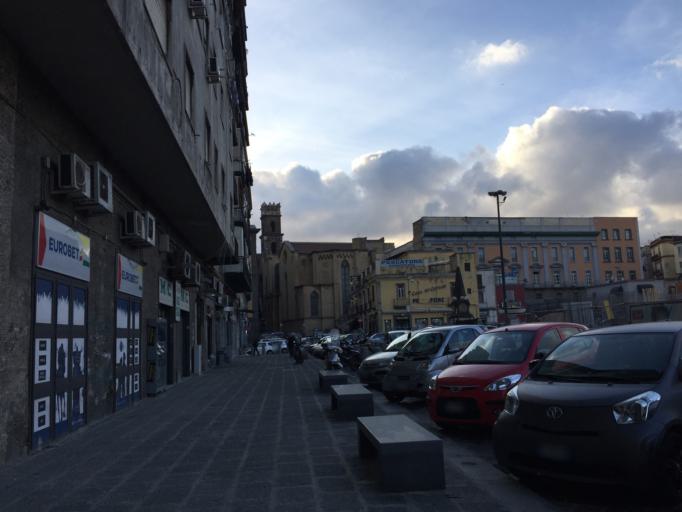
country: IT
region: Campania
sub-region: Provincia di Napoli
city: Napoli
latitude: 40.8468
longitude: 14.2661
